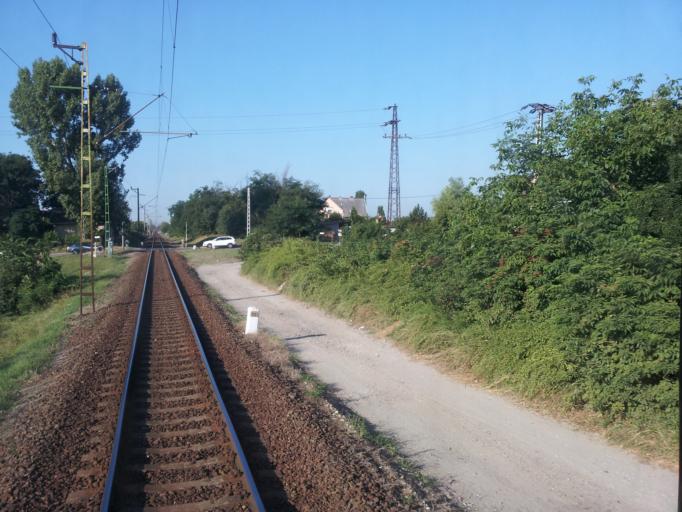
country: HU
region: Pest
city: Dunaharaszti
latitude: 47.3622
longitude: 19.1042
